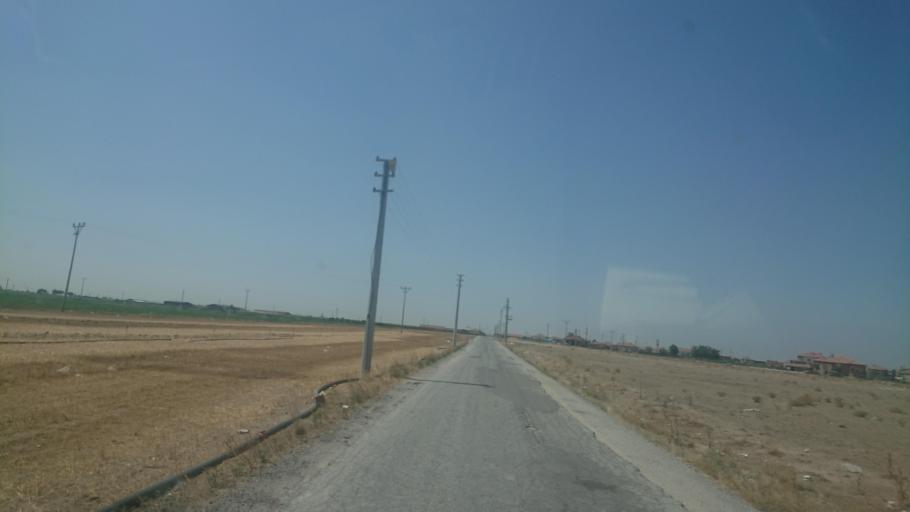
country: TR
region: Aksaray
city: Yesilova
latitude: 38.2914
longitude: 33.7204
